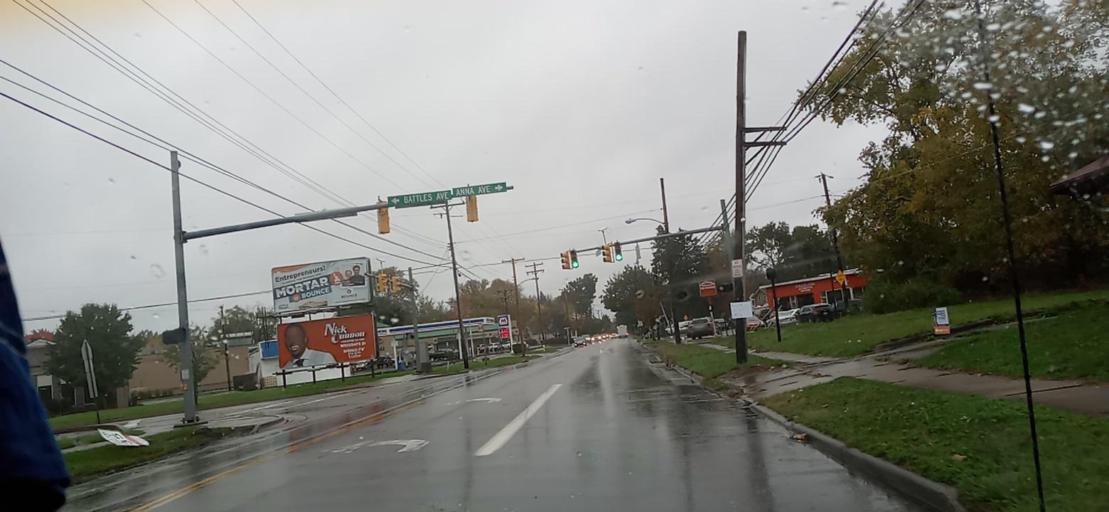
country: US
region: Ohio
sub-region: Summit County
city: Barberton
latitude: 41.0471
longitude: -81.5701
